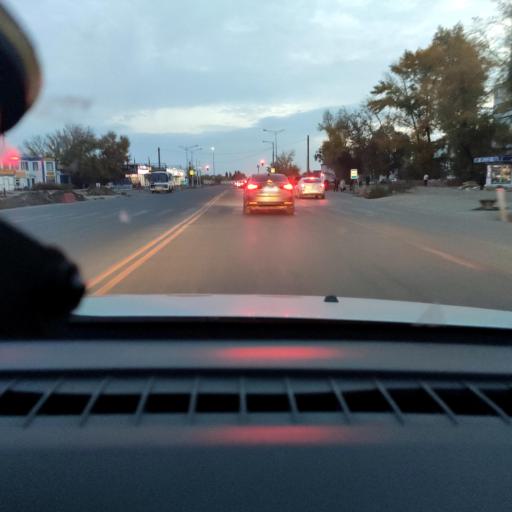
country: RU
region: Samara
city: Samara
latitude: 53.1255
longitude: 50.0895
